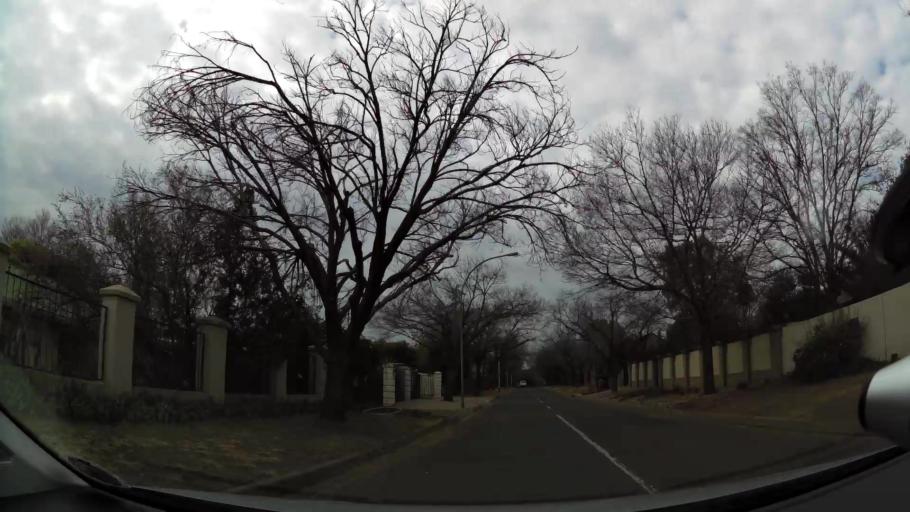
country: ZA
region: Orange Free State
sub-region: Mangaung Metropolitan Municipality
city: Bloemfontein
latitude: -29.0910
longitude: 26.2101
